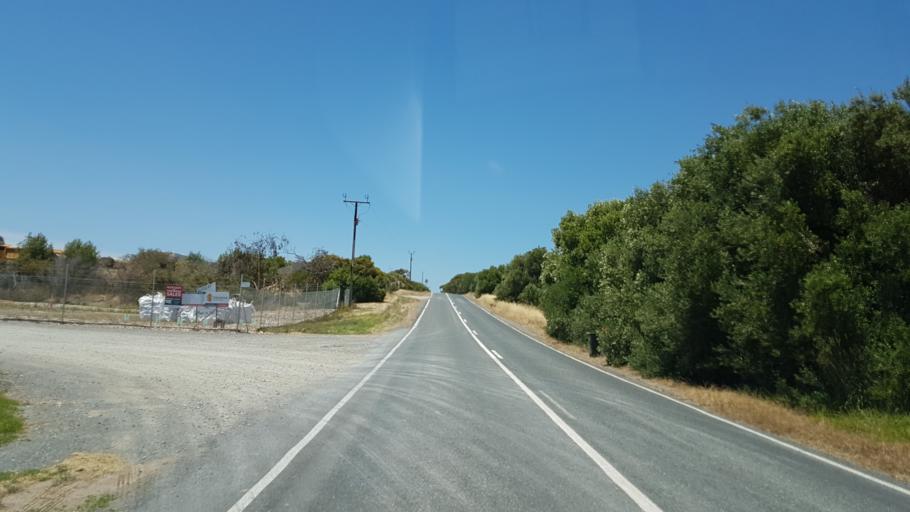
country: AU
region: South Australia
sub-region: Onkaparinga
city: Moana
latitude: -35.2325
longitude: 138.4943
